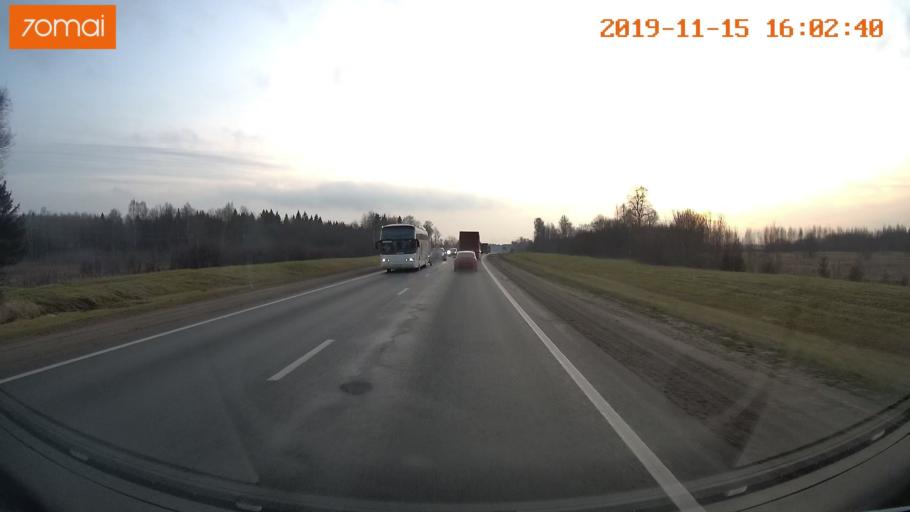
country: RU
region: Jaroslavl
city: Yaroslavl
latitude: 57.7687
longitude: 39.9226
